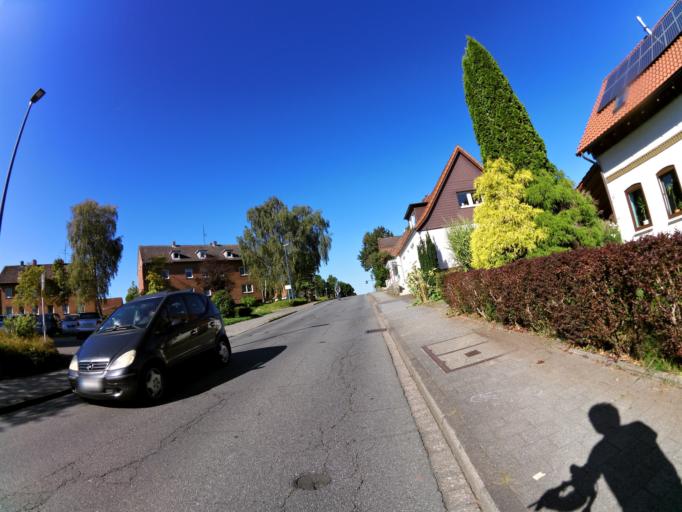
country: DE
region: Schleswig-Holstein
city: Eckernforde
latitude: 54.4814
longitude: 9.8343
